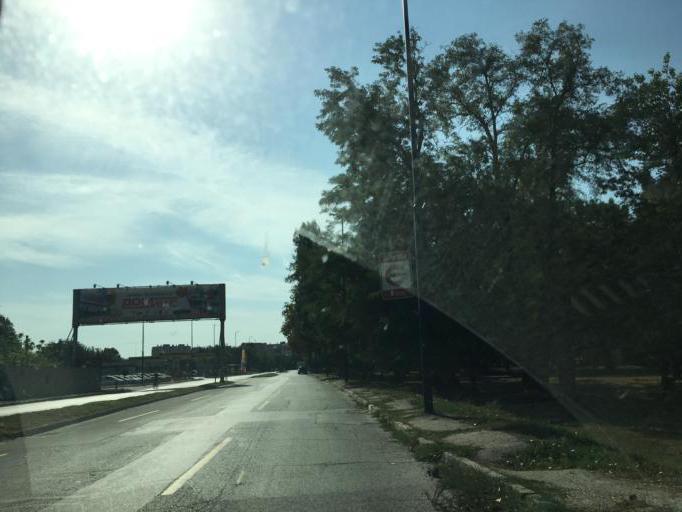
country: BG
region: Pazardzhik
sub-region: Obshtina Pazardzhik
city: Pazardzhik
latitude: 42.2092
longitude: 24.3258
